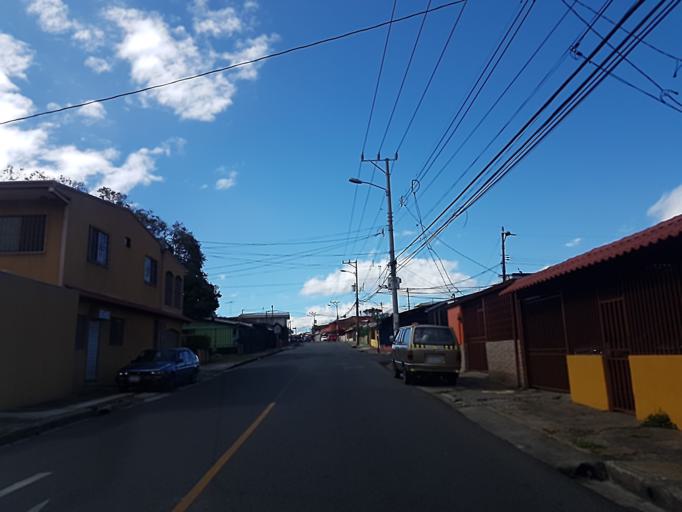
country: CR
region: San Jose
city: San Felipe
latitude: 9.9199
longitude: -84.0967
